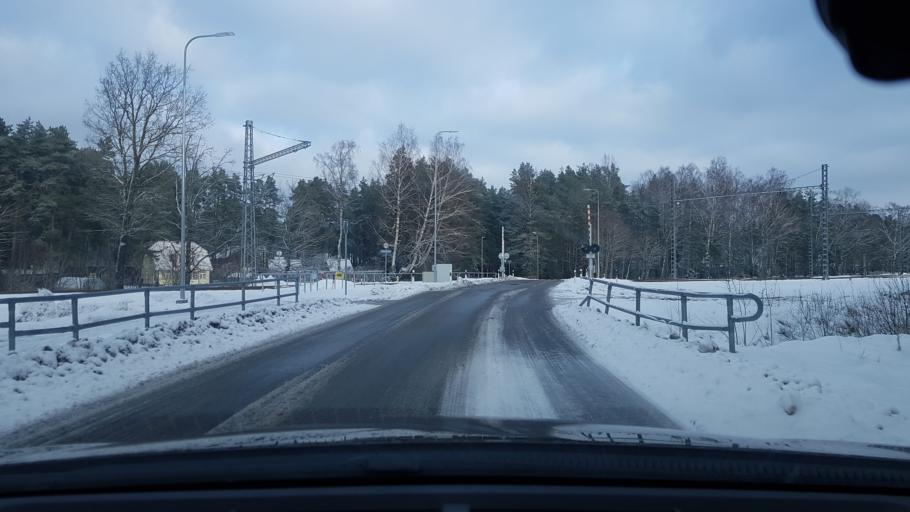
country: EE
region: Harju
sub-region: Keila linn
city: Keila
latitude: 59.3204
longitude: 24.2522
